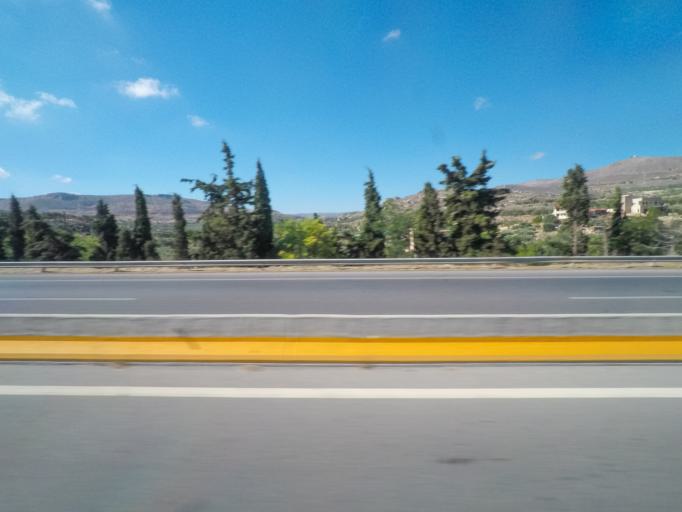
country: GR
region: Crete
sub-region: Nomos Irakleiou
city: Gournes
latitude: 35.3241
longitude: 25.2807
